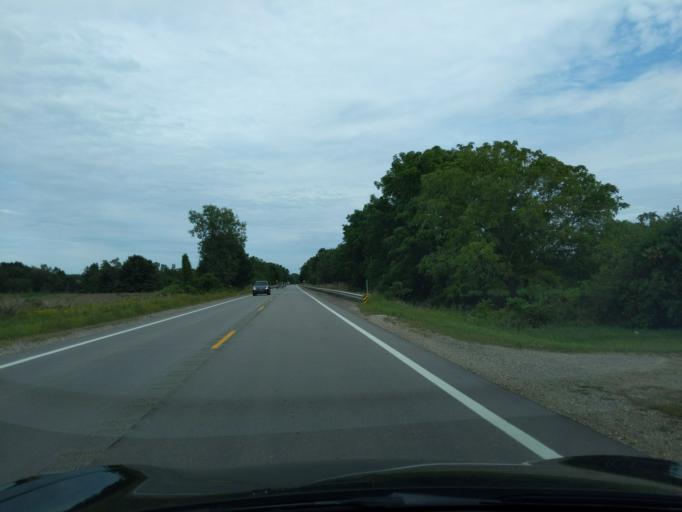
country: US
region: Michigan
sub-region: Barry County
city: Nashville
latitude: 42.5673
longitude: -85.0260
